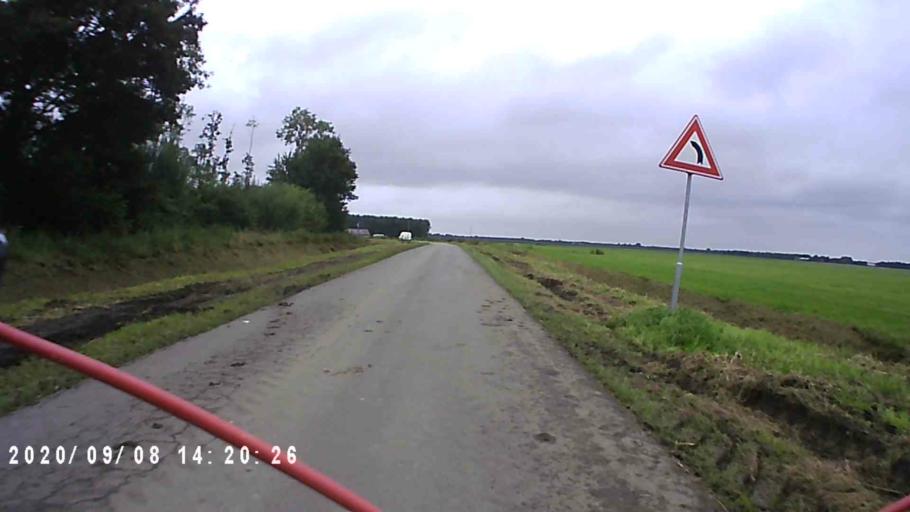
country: NL
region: Groningen
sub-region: Gemeente Slochteren
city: Slochteren
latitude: 53.2101
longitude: 6.8477
